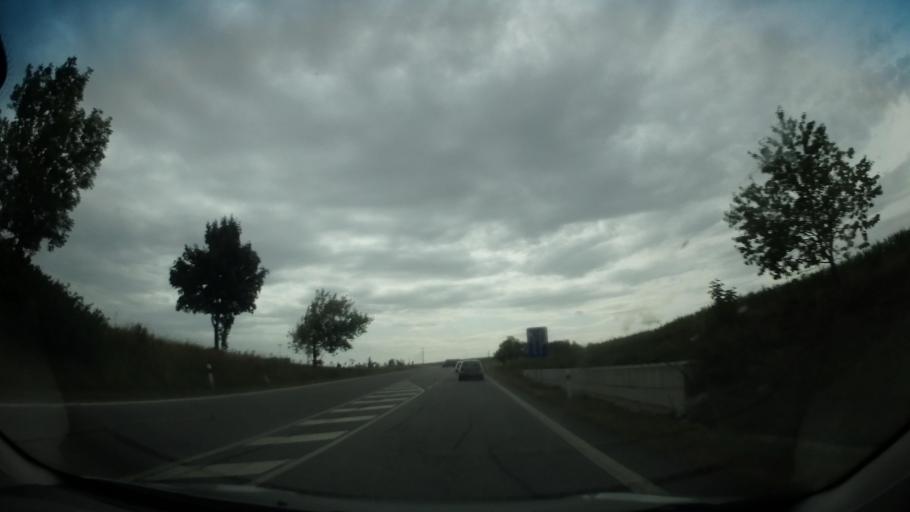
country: CZ
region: Vysocina
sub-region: Okres Zd'ar nad Sazavou
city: Zd'ar nad Sazavou
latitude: 49.5591
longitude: 15.9739
